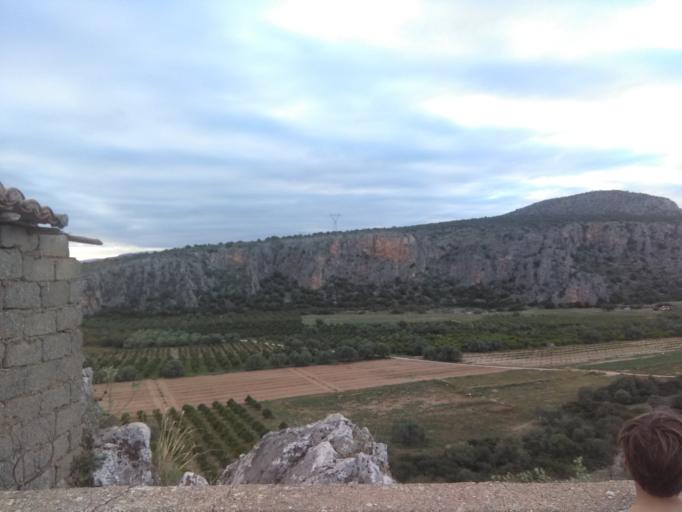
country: GR
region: Peloponnese
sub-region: Nomos Argolidos
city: Drepanon
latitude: 37.5312
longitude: 22.9625
